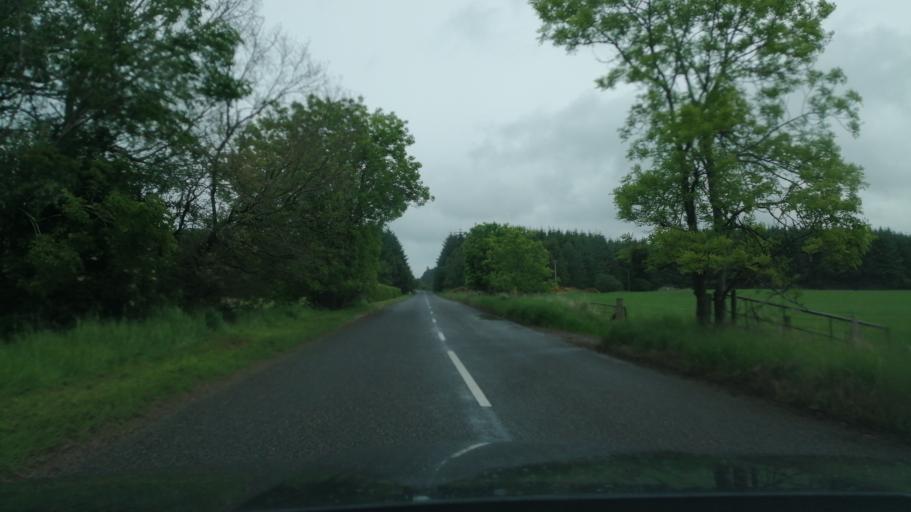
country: GB
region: Scotland
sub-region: Aberdeenshire
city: Portsoy
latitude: 57.6210
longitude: -2.7221
